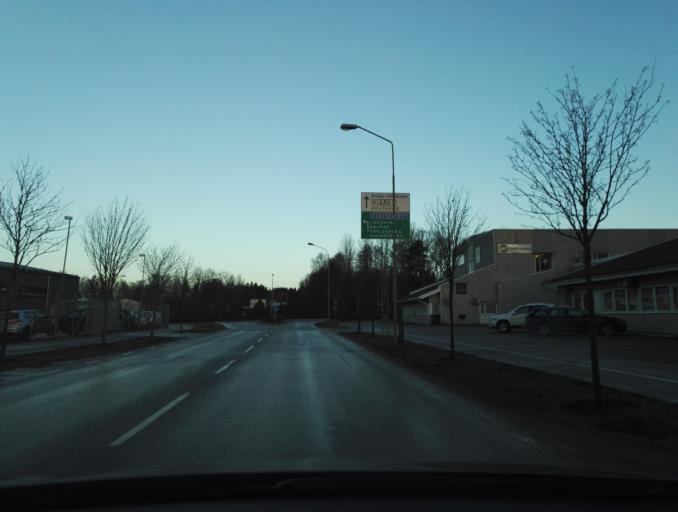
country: SE
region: Kronoberg
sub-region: Vaxjo Kommun
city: Vaexjoe
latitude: 56.8944
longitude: 14.7820
